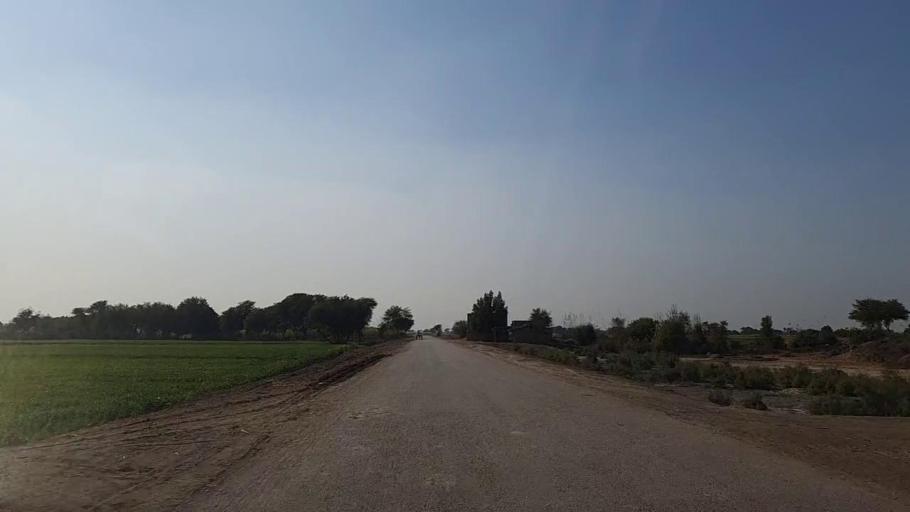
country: PK
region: Sindh
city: Daur
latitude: 26.4043
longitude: 68.2919
